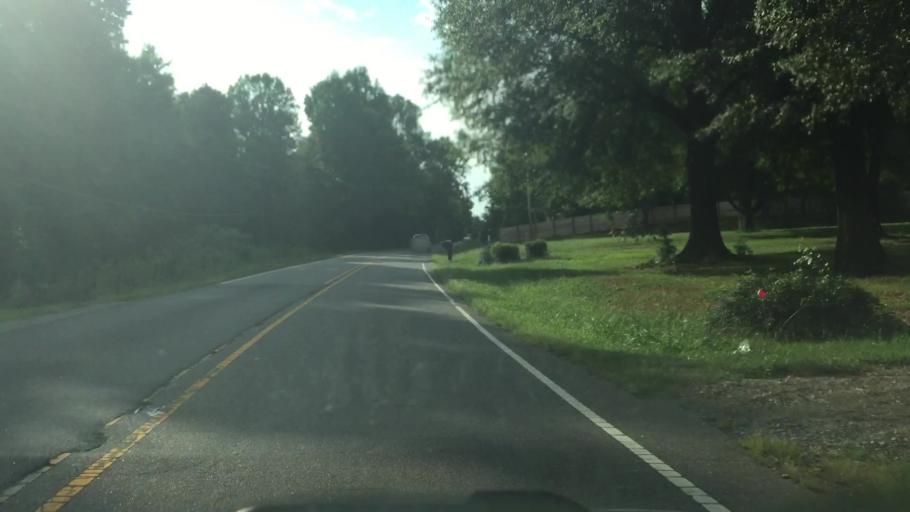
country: US
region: North Carolina
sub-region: Iredell County
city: Mooresville
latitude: 35.5552
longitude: -80.7823
